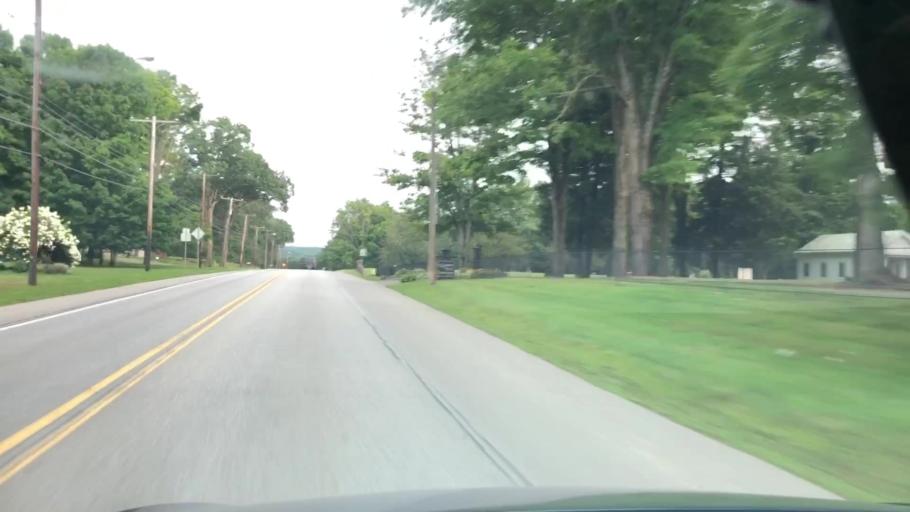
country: US
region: Pennsylvania
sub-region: Crawford County
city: Titusville
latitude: 41.6449
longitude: -79.7149
